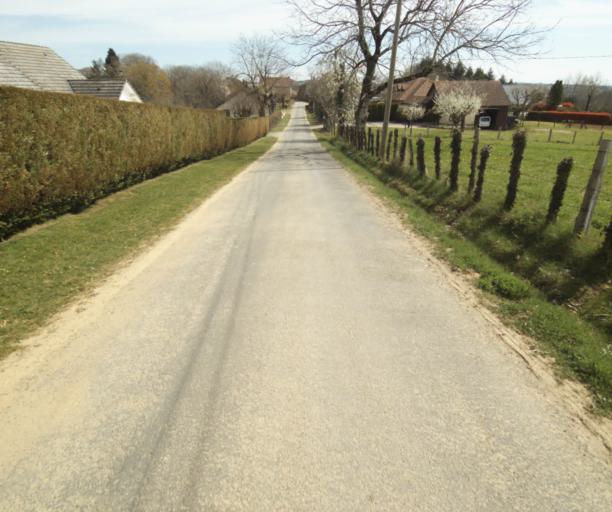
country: FR
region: Limousin
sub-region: Departement de la Correze
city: Naves
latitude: 45.3403
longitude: 1.7711
